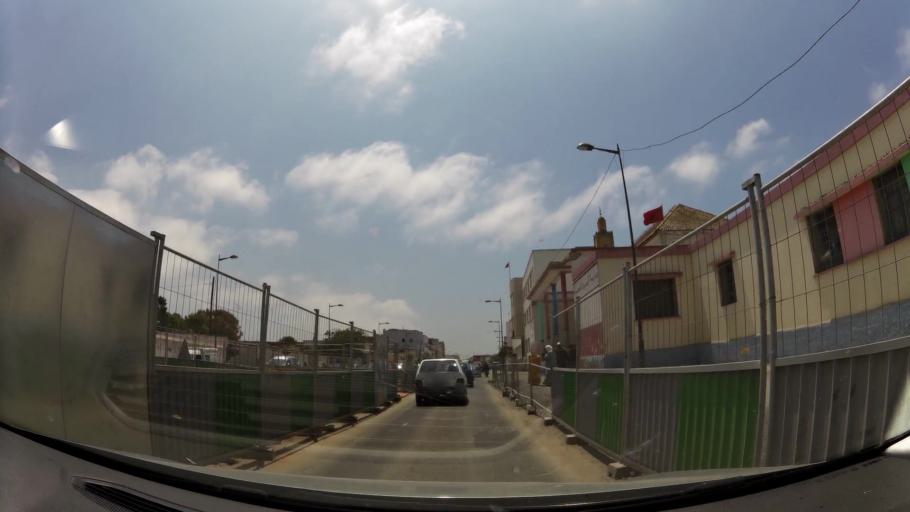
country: MA
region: Rabat-Sale-Zemmour-Zaer
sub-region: Rabat
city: Rabat
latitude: 34.0080
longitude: -6.8617
